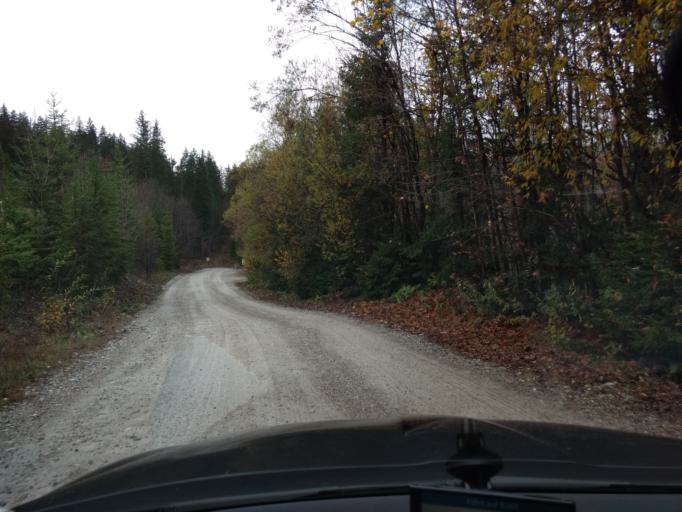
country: DE
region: Bavaria
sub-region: Upper Bavaria
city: Jachenau
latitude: 47.5588
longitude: 11.4911
